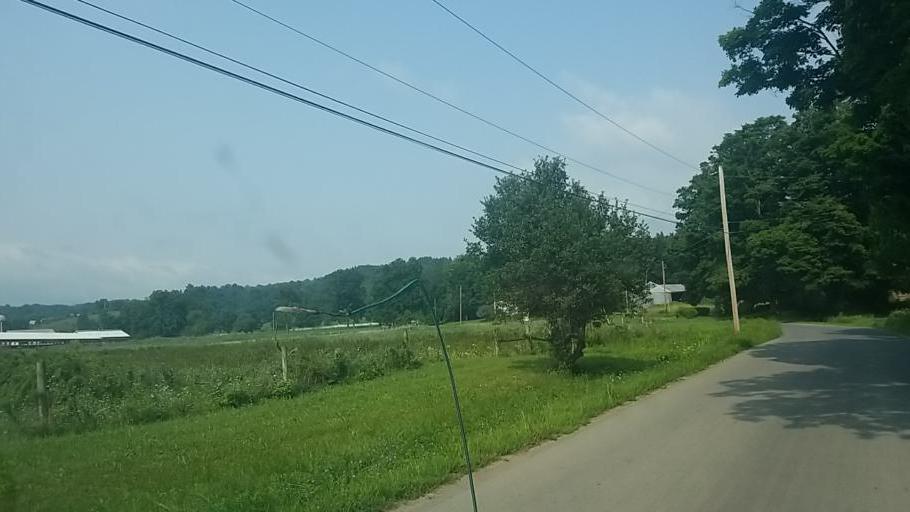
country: US
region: New York
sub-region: Montgomery County
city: Fonda
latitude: 42.9492
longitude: -74.4336
